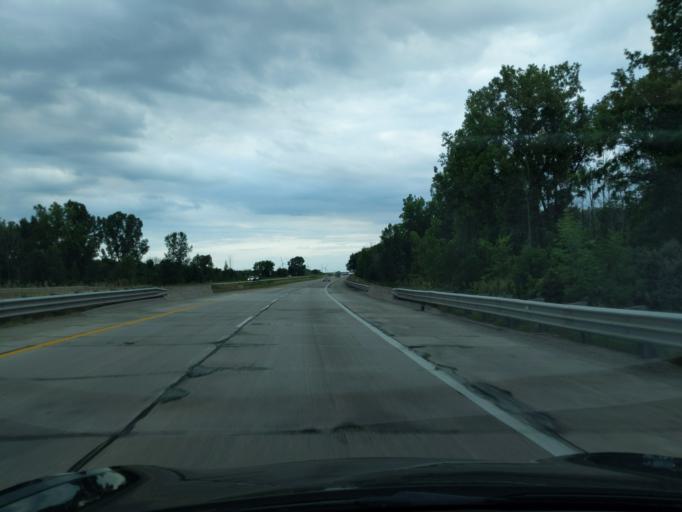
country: US
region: Michigan
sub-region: Isabella County
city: Shepherd
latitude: 43.5348
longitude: -84.6770
